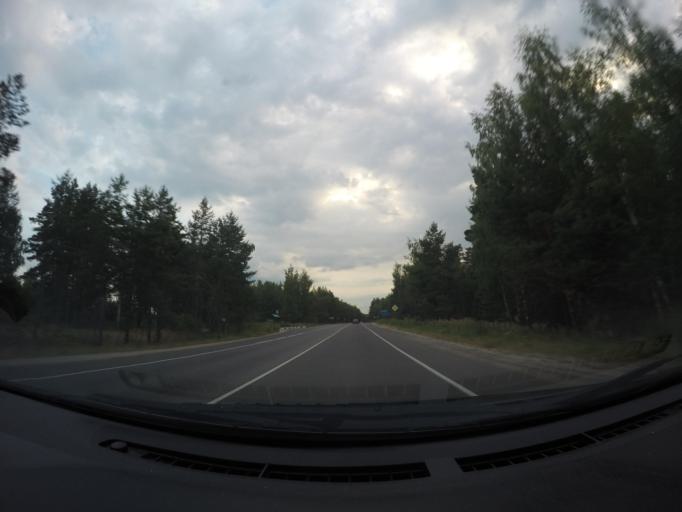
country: RU
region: Moskovskaya
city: Krasnyy Tkach
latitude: 55.4077
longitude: 39.1579
